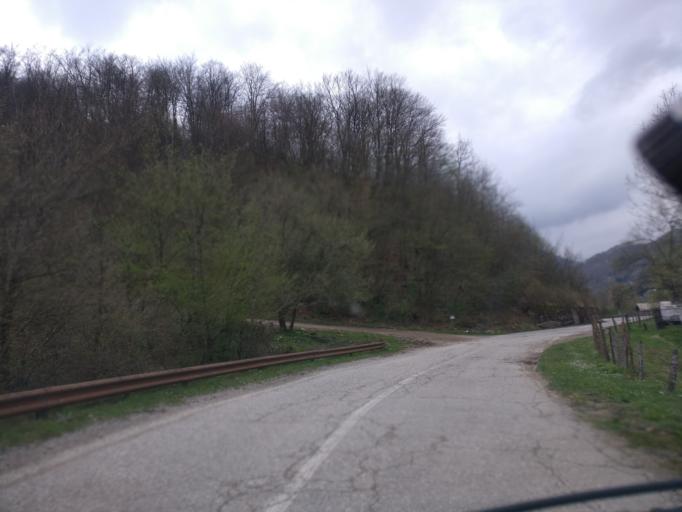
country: BA
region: Republika Srpska
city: Foca
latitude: 43.4734
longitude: 18.7515
